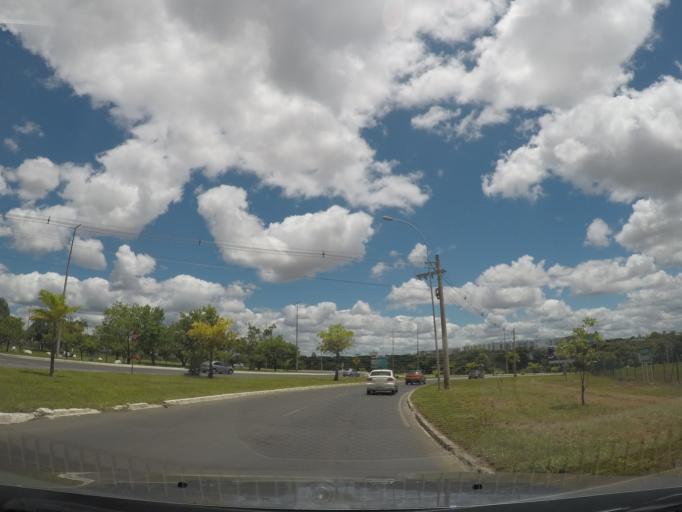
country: BR
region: Federal District
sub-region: Brasilia
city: Brasilia
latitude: -15.8376
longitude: -47.9663
